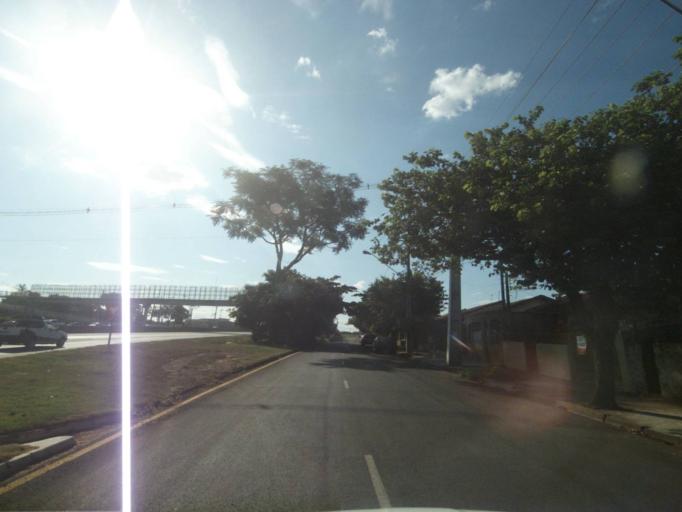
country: BR
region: Parana
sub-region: Londrina
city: Londrina
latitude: -23.3594
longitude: -51.1539
